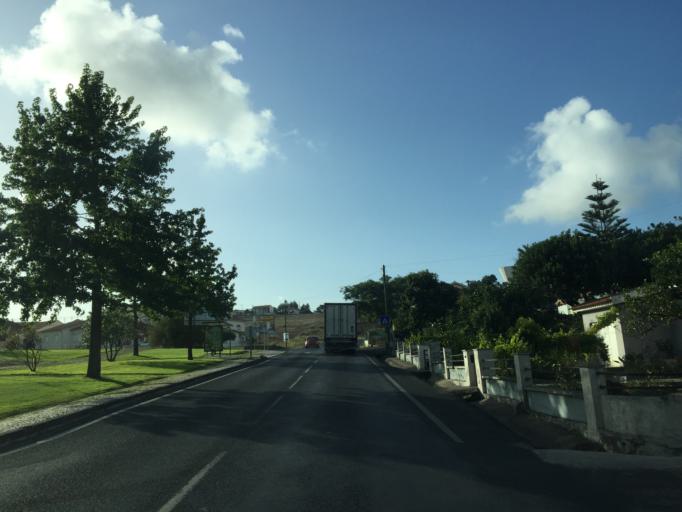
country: PT
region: Lisbon
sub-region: Torres Vedras
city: Torres Vedras
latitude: 39.1081
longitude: -9.2620
